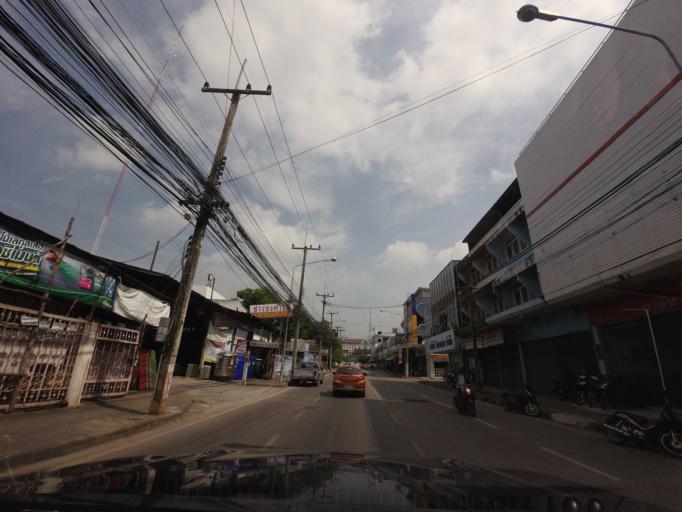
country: TH
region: Khon Kaen
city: Khon Kaen
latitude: 16.4383
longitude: 102.8305
